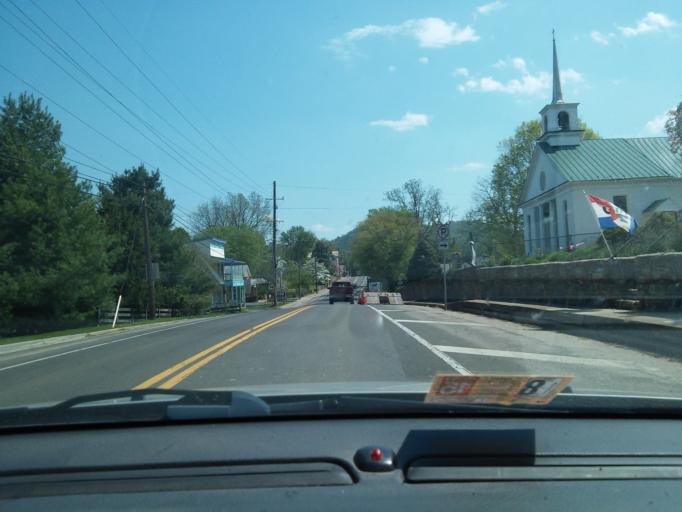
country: US
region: Virginia
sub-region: Rappahannock County
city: Washington
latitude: 38.7661
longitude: -78.1007
